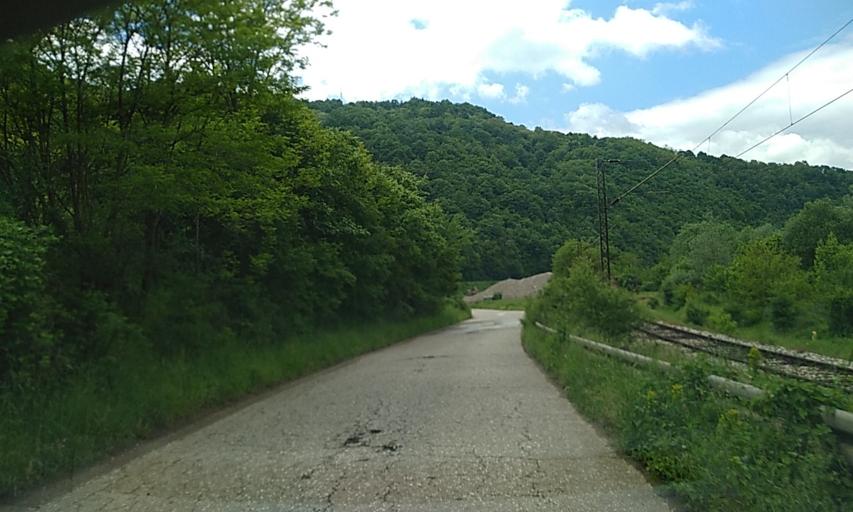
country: RS
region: Central Serbia
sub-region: Pcinjski Okrug
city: Vladicin Han
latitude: 42.7335
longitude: 22.0590
